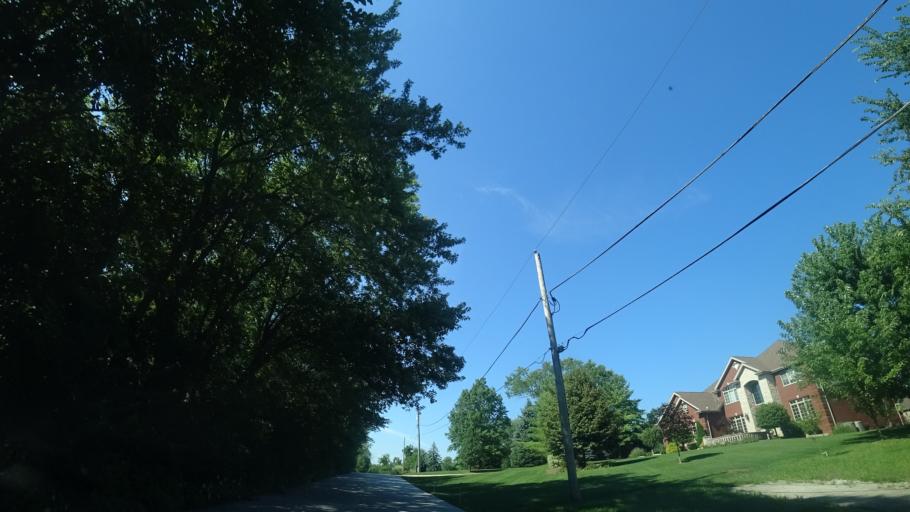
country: US
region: Illinois
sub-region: Cook County
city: Orland Hills
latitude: 41.5742
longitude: -87.8870
